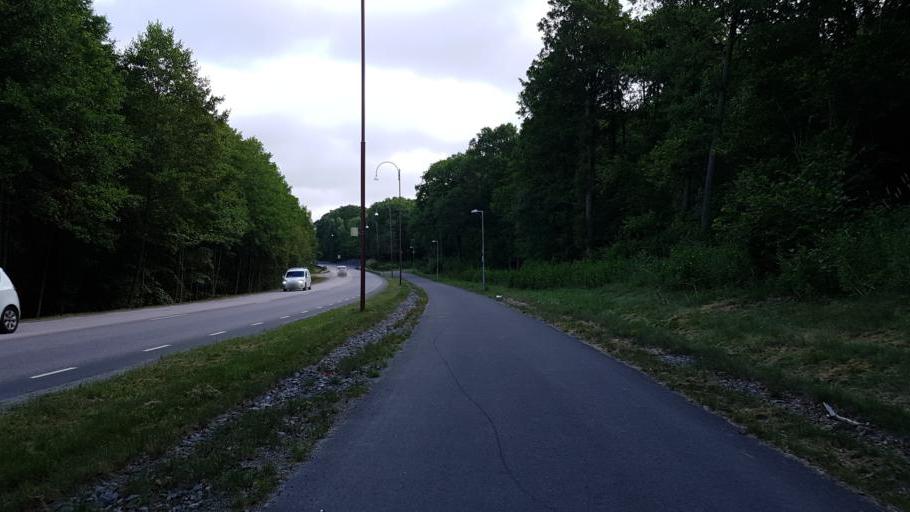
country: SE
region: Vaestra Goetaland
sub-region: Harryda Kommun
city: Molnlycke
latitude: 57.6646
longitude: 12.0924
